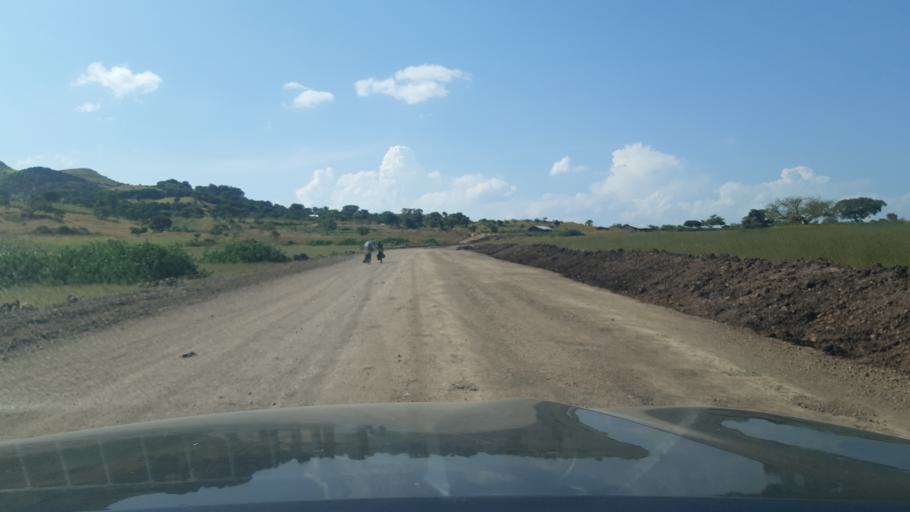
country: ET
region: Amhara
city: Dabat
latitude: 13.1588
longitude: 37.6093
